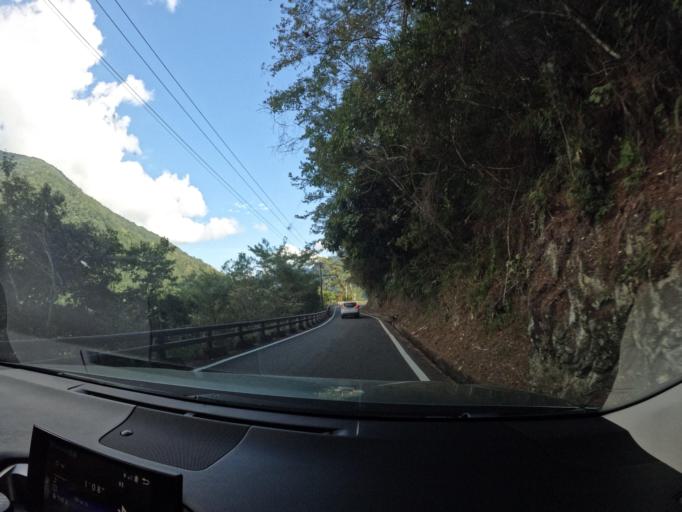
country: TW
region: Taiwan
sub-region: Taitung
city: Taitung
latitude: 23.1785
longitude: 121.0432
